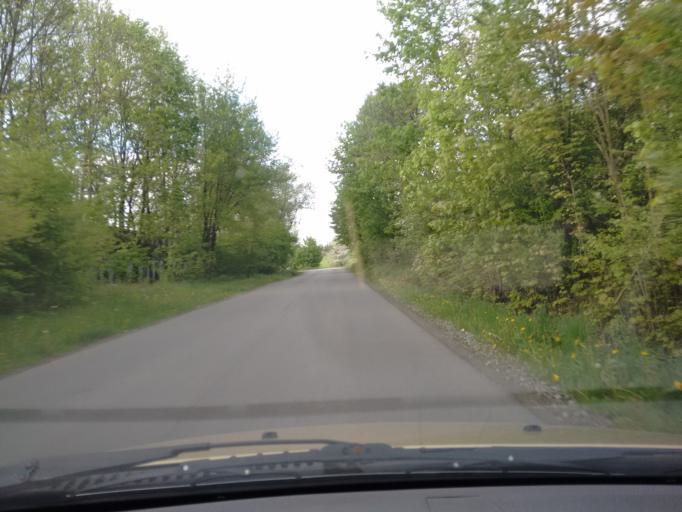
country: PL
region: Silesian Voivodeship
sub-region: Powiat cieszynski
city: Puncow
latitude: 49.7469
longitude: 18.6705
